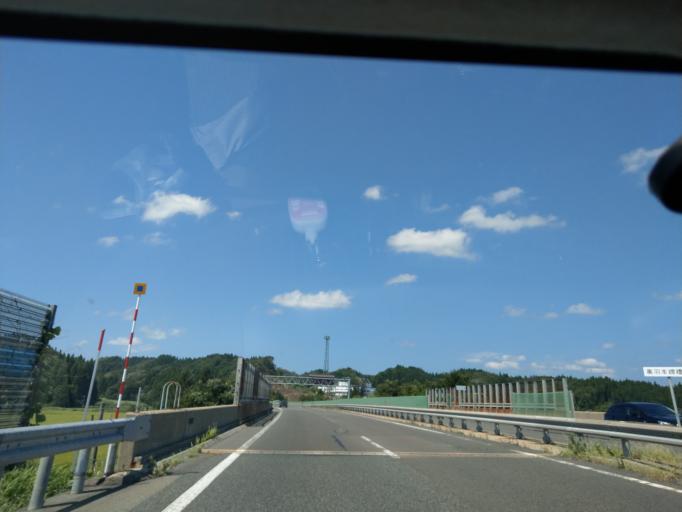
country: JP
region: Akita
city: Akita
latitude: 39.6496
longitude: 140.2065
